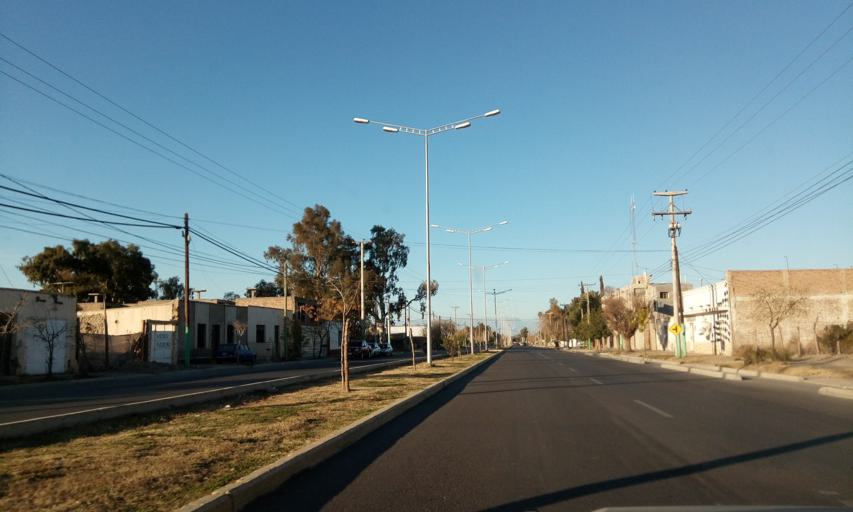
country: AR
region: San Juan
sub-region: Departamento de Rivadavia
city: Rivadavia
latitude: -31.5245
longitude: -68.6255
